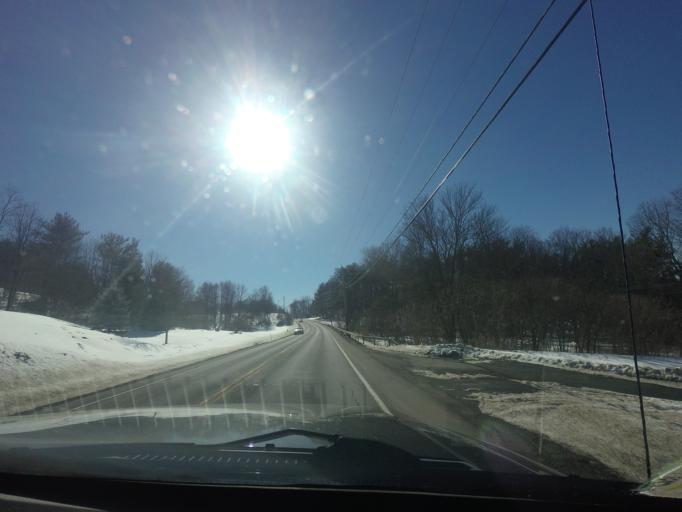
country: US
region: New York
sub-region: Saratoga County
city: Waterford
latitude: 42.8188
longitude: -73.6322
